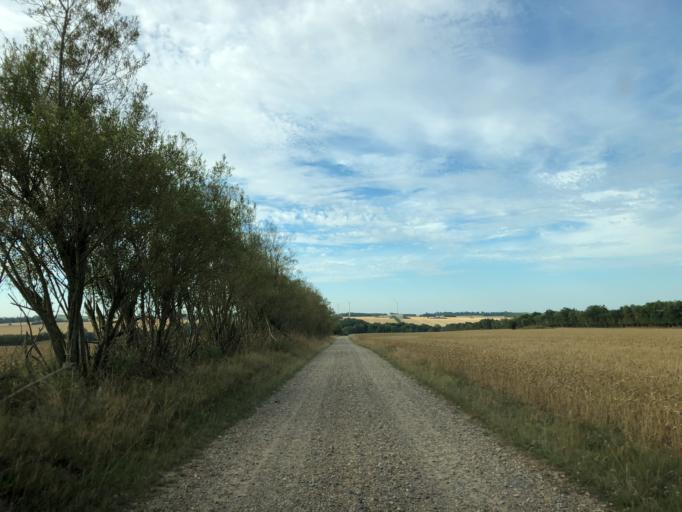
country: DK
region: Central Jutland
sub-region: Ringkobing-Skjern Kommune
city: Skjern
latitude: 56.0764
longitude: 8.4230
